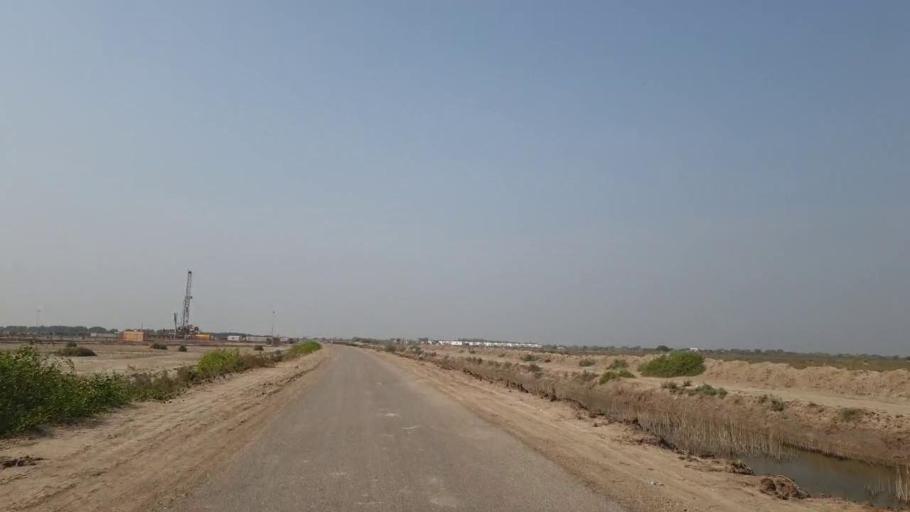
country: PK
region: Sindh
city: Tando Muhammad Khan
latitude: 24.9667
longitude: 68.5134
